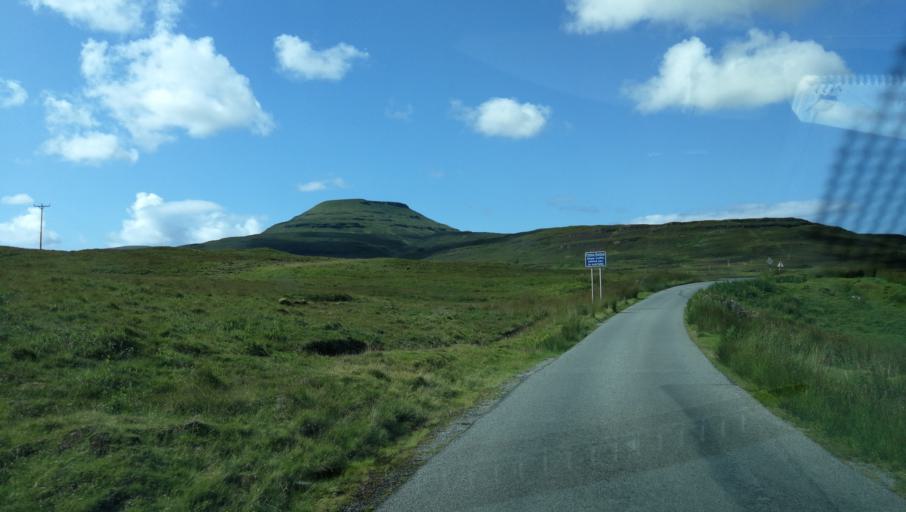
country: GB
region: Scotland
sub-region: Highland
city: Isle of Skye
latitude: 57.4212
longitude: -6.5815
